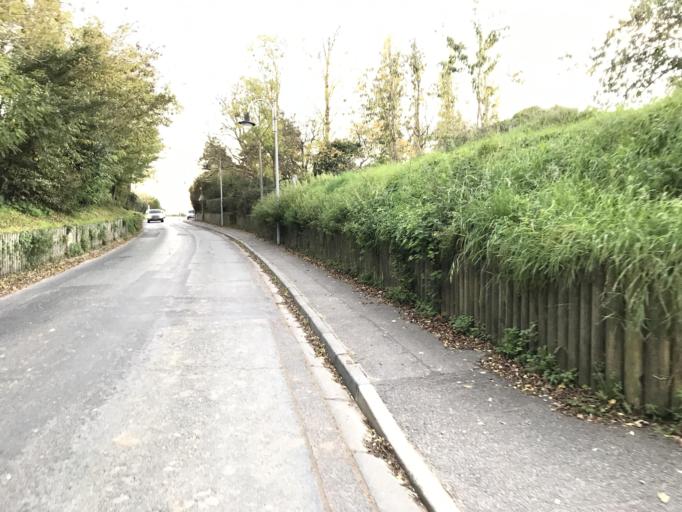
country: FR
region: Ile-de-France
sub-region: Departement de l'Essonne
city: Saulx-les-Chartreux
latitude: 48.6842
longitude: 2.2782
